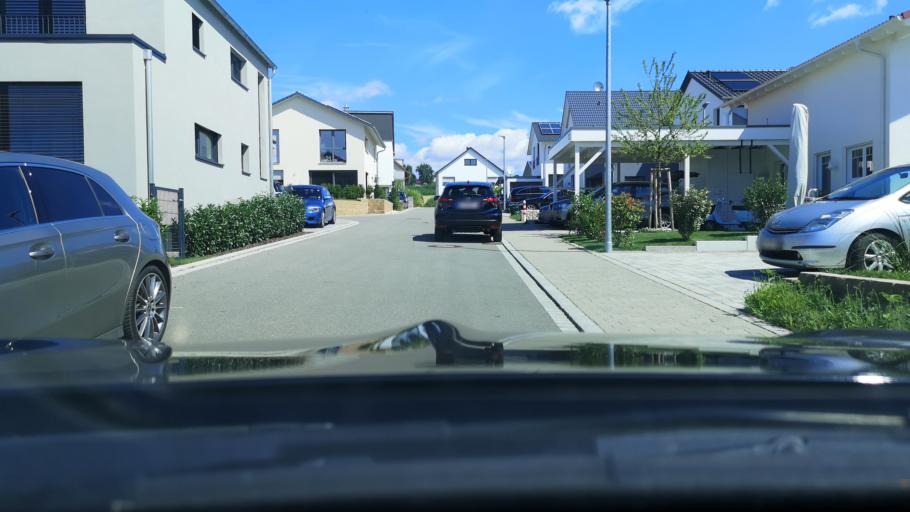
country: DE
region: Baden-Wuerttemberg
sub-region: Regierungsbezirk Stuttgart
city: Altenriet
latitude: 48.5929
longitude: 9.1812
